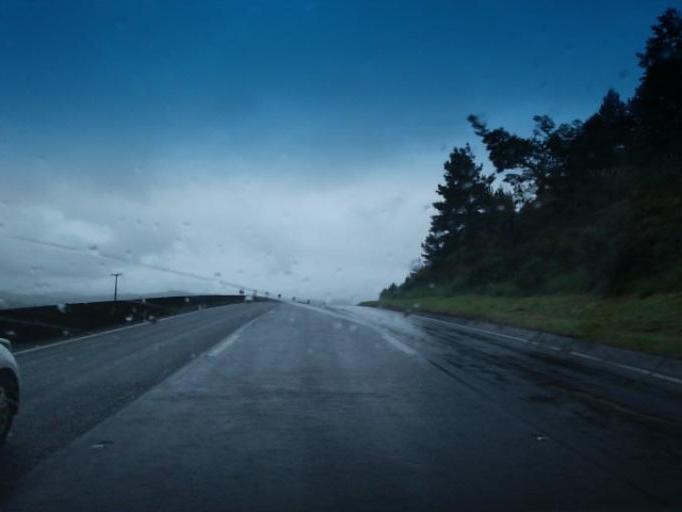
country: BR
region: Parana
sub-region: Campina Grande Do Sul
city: Campina Grande do Sul
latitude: -25.1613
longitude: -48.8617
